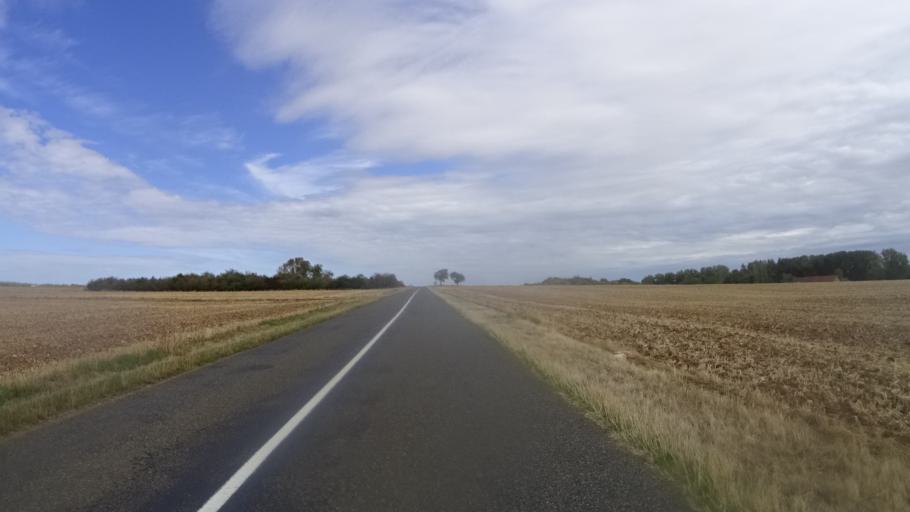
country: FR
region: Centre
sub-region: Departement du Loiret
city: Malesherbes
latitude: 48.2107
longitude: 2.4153
